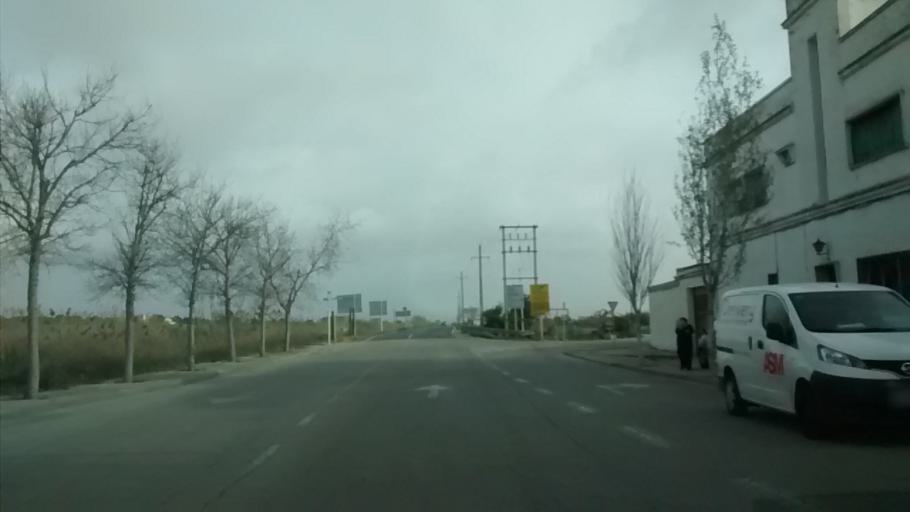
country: ES
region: Catalonia
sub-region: Provincia de Tarragona
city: Sant Carles de la Rapita
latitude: 40.6218
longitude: 0.5990
